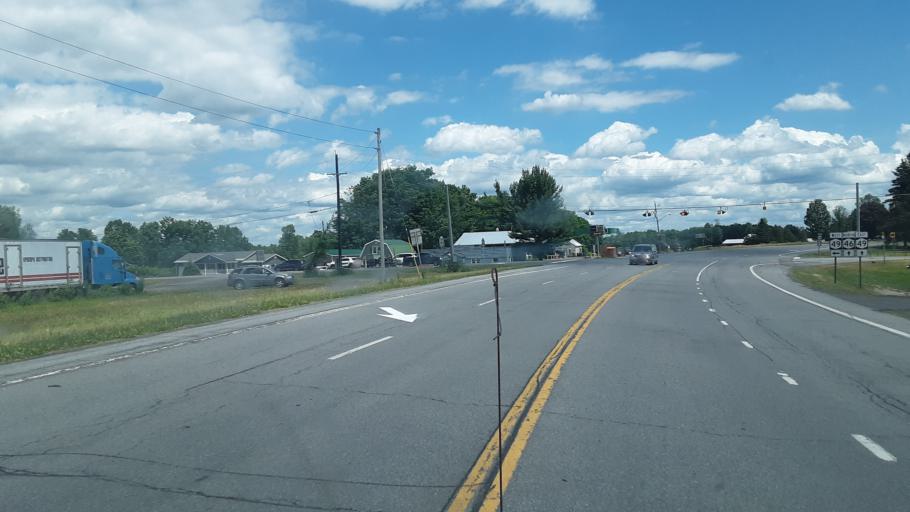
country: US
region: New York
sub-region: Madison County
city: Oneida
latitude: 43.2099
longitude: -75.5902
